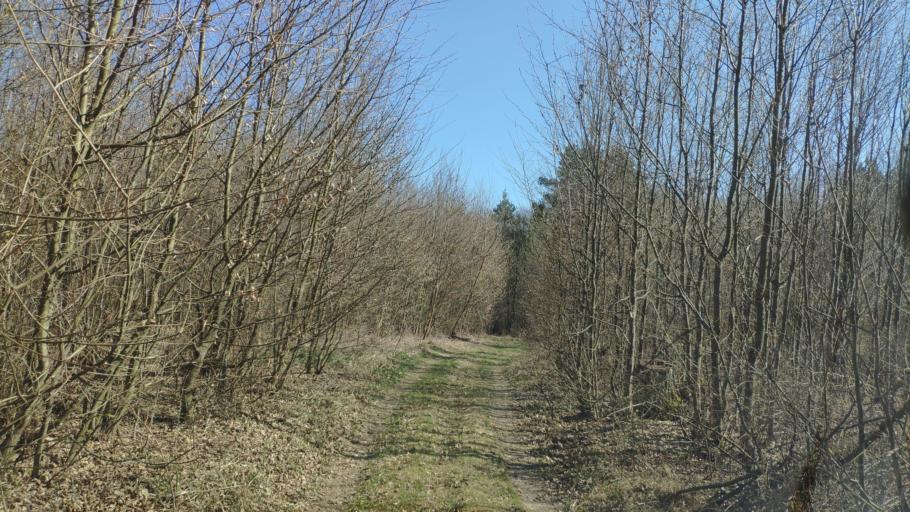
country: SK
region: Kosicky
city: Moldava nad Bodvou
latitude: 48.5612
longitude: 20.9327
